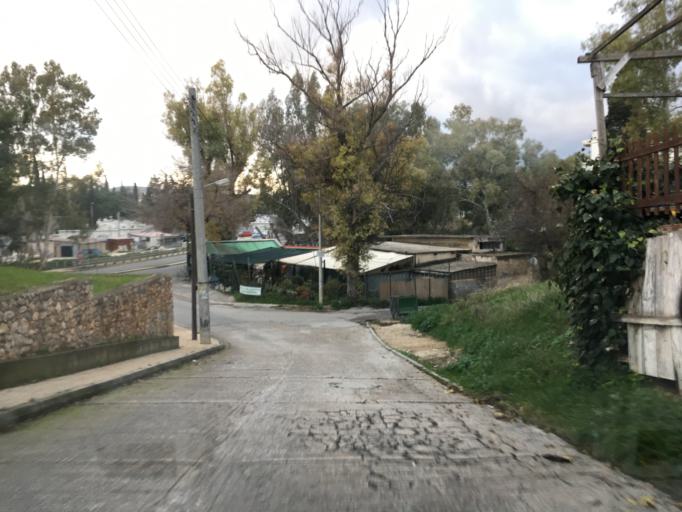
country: GR
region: Attica
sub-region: Nomarchia Athinas
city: Nea Filadelfeia
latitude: 38.0493
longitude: 23.7384
